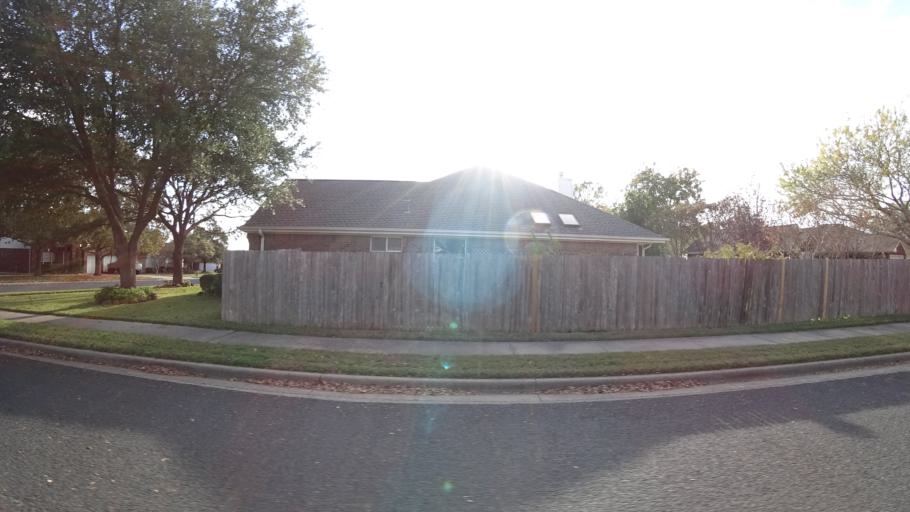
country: US
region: Texas
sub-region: Williamson County
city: Brushy Creek
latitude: 30.5078
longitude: -97.7304
